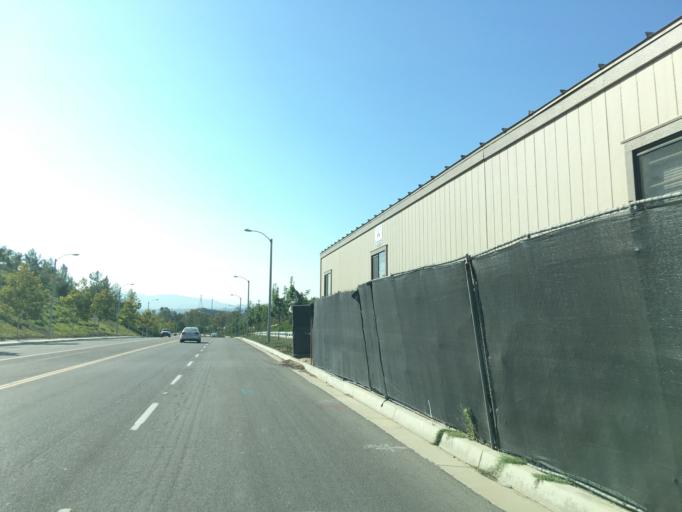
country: US
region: California
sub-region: Los Angeles County
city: Val Verde
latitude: 34.4547
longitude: -118.6335
